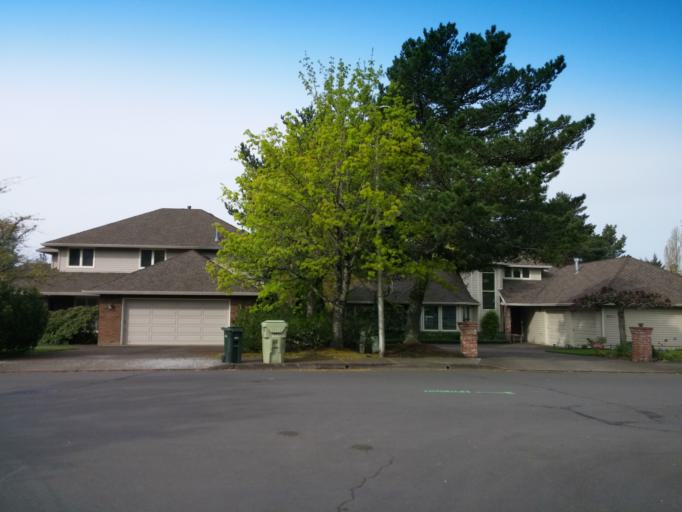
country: US
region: Oregon
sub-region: Washington County
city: Cedar Mill
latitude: 45.5401
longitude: -122.8131
